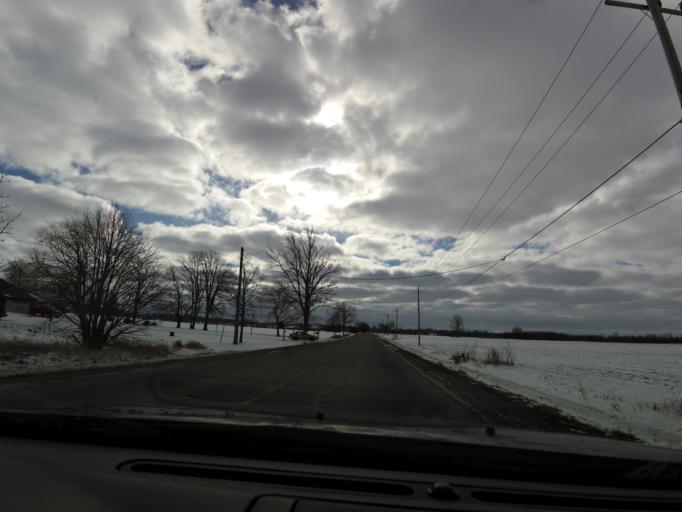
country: CA
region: Ontario
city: Hamilton
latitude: 43.1281
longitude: -79.6529
